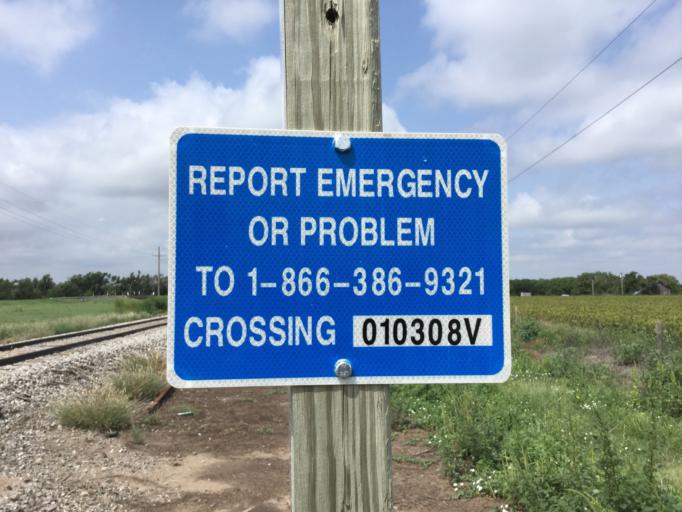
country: US
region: Kansas
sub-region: Rush County
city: La Crosse
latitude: 38.4670
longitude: -99.5576
